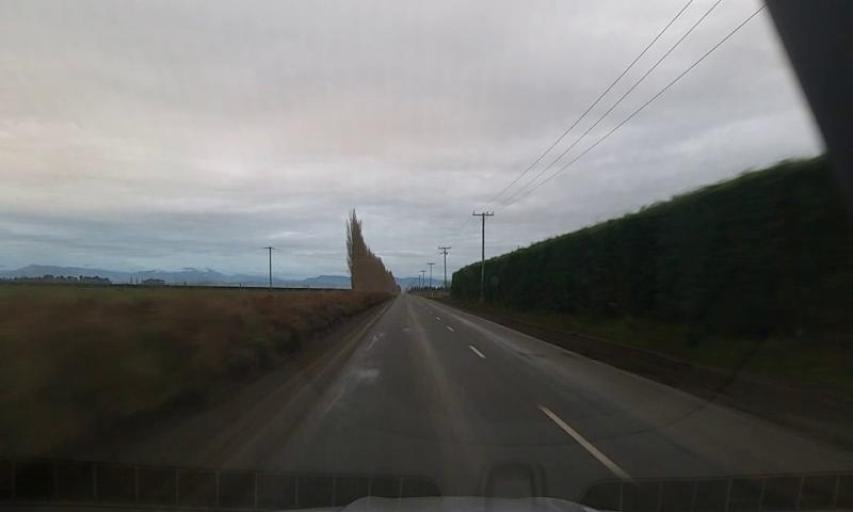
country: NZ
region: Canterbury
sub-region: Ashburton District
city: Methven
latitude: -43.7419
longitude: 171.7119
